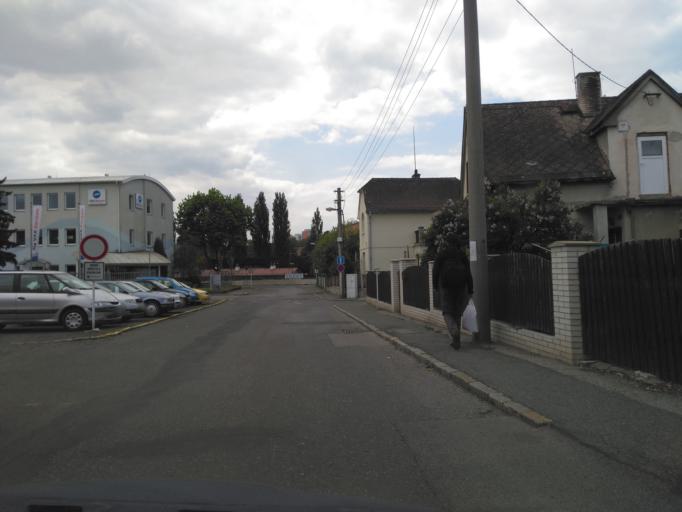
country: CZ
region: Central Bohemia
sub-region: Okres Beroun
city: Beroun
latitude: 49.9698
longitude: 14.0767
